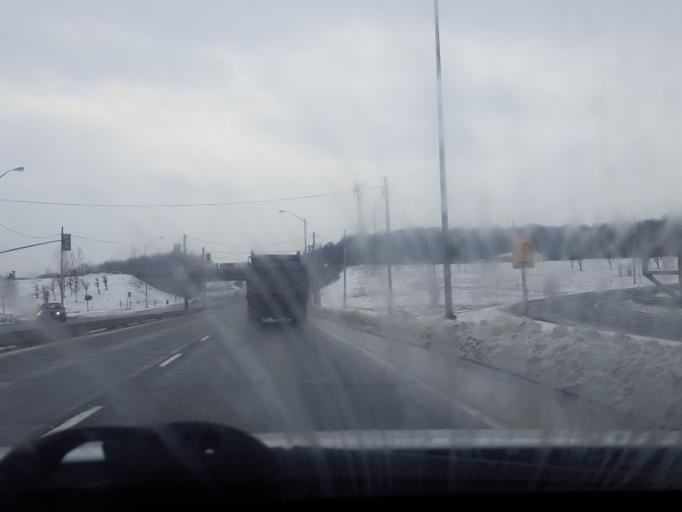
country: CA
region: Ontario
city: Newmarket
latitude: 43.9786
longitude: -79.3898
